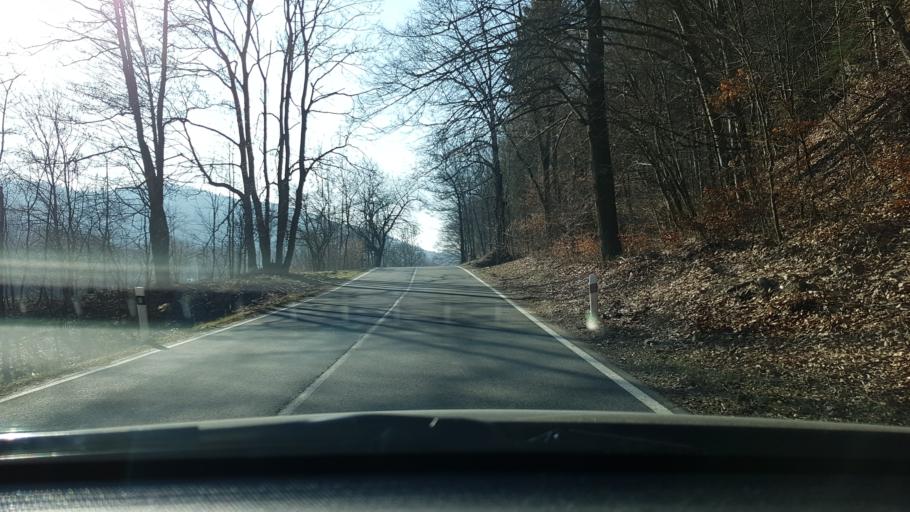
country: CZ
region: Olomoucky
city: Dolni Bohdikov
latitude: 50.0073
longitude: 16.8948
